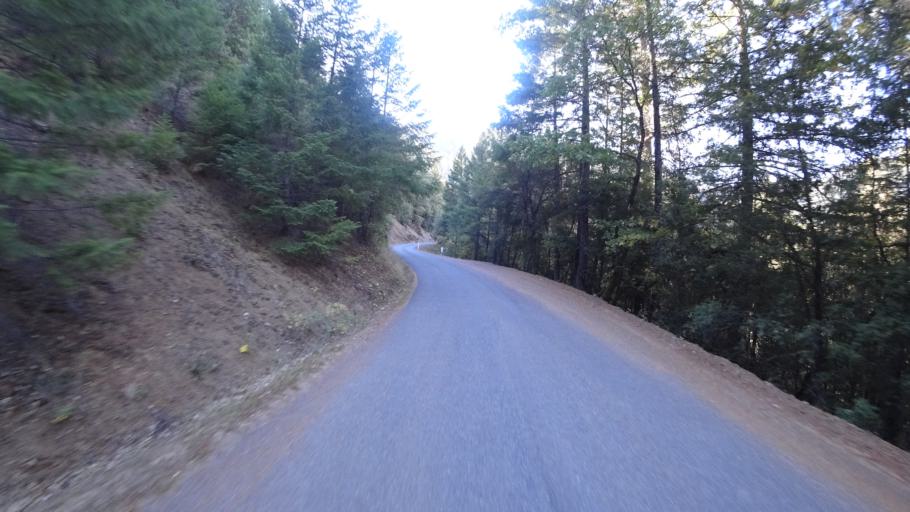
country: US
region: California
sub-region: Humboldt County
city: Willow Creek
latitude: 41.1525
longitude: -123.2090
